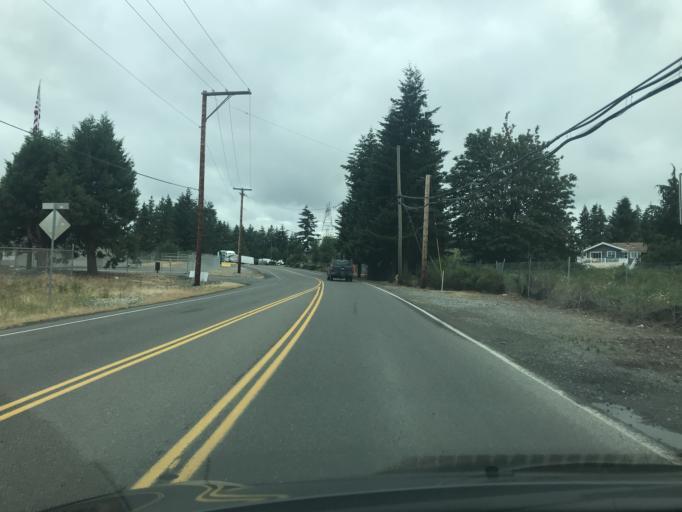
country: US
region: Washington
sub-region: King County
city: Covington
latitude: 47.3501
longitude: -122.1187
